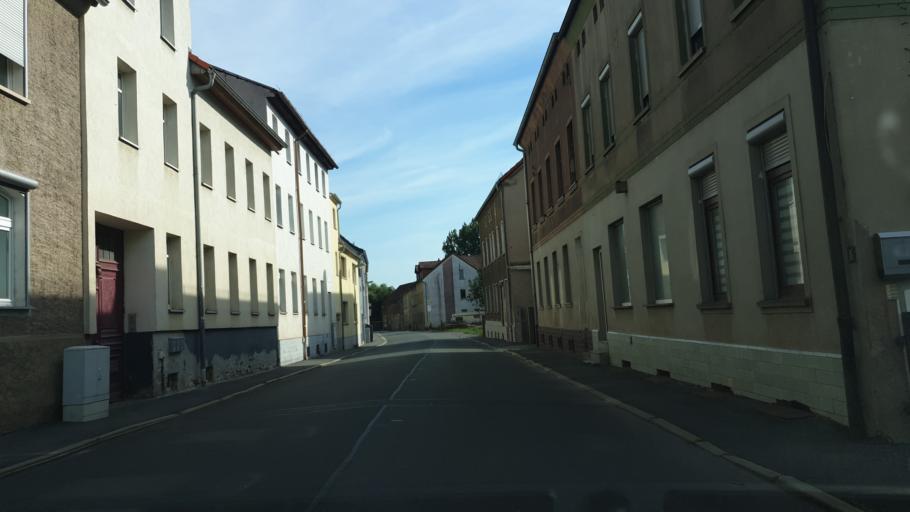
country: DE
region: Thuringia
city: Gera
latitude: 50.8371
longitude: 12.0783
